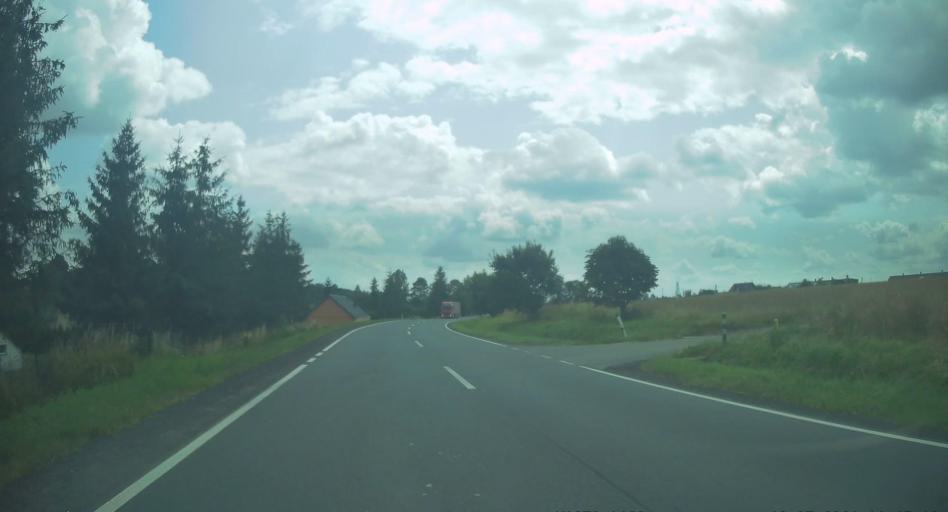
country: PL
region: Opole Voivodeship
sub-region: Powiat prudnicki
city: Laka Prudnicka
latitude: 50.3788
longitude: 17.5314
